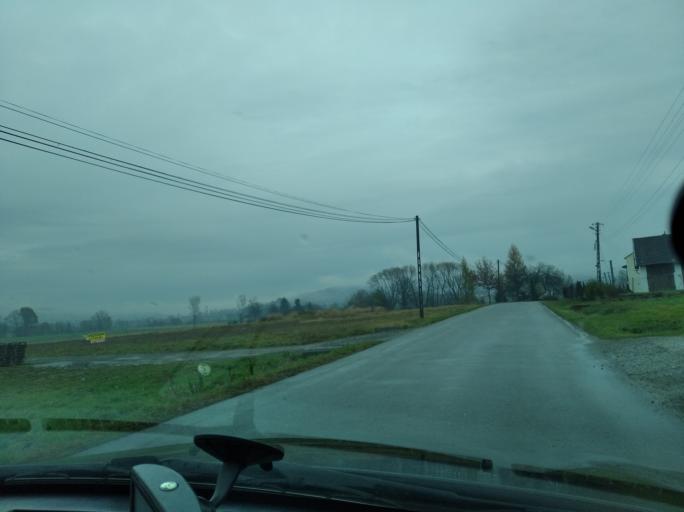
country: PL
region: Subcarpathian Voivodeship
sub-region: Powiat strzyzowski
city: Babica
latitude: 49.9281
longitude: 21.8543
